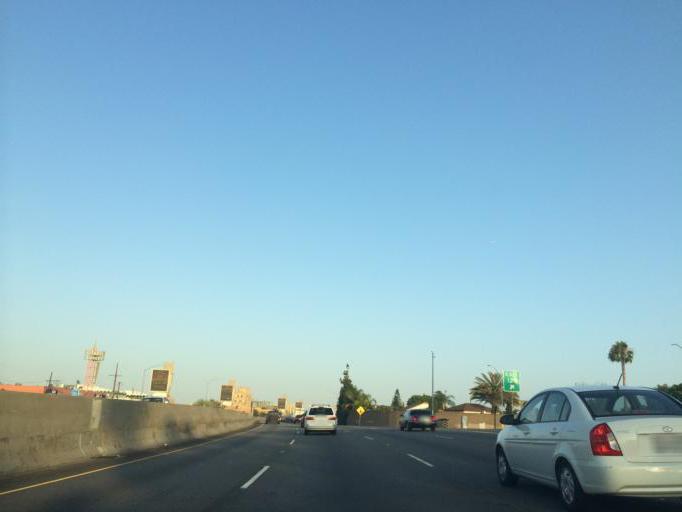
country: US
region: California
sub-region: Los Angeles County
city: Commerce
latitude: 34.0079
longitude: -118.1578
